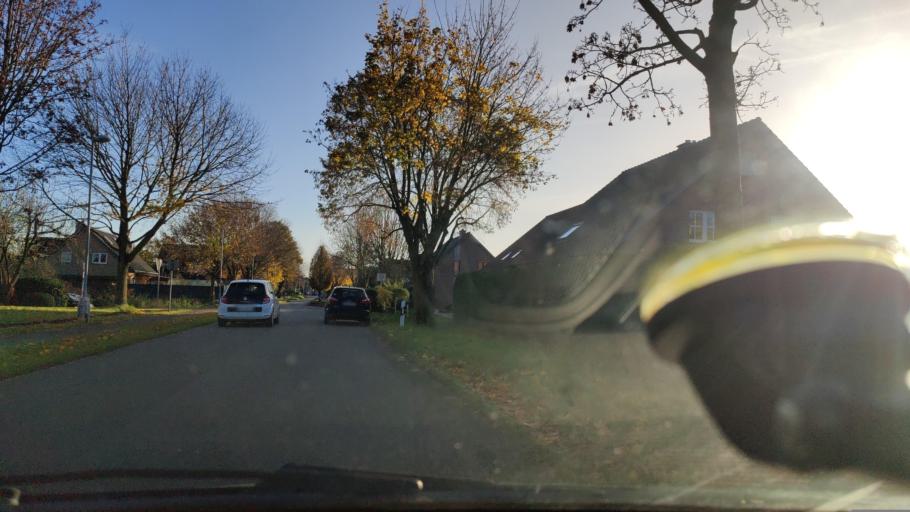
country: DE
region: North Rhine-Westphalia
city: Straelen
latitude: 51.4513
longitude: 6.2657
